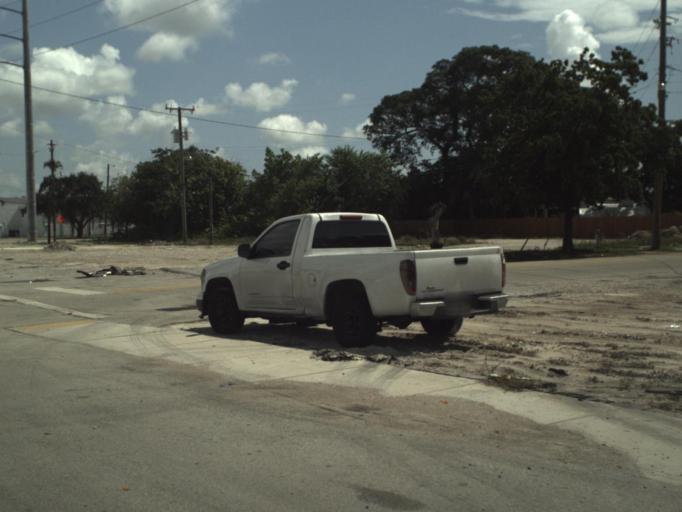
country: US
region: Florida
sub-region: Broward County
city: Pembroke Pines
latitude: 26.0156
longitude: -80.2078
